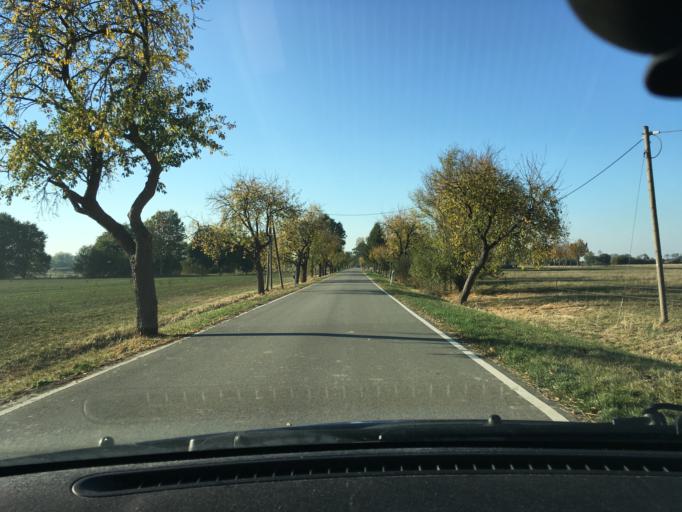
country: DE
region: Lower Saxony
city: Hitzacker
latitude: 53.1875
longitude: 11.0117
